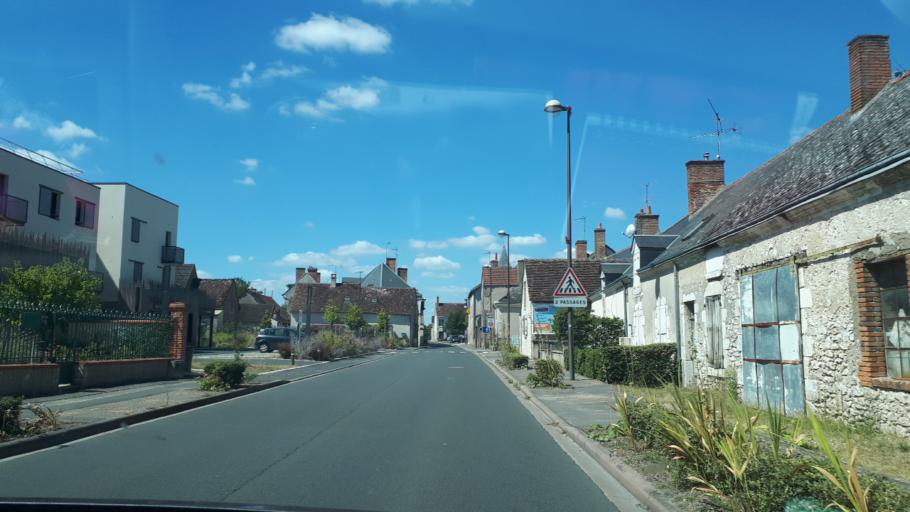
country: FR
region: Centre
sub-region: Departement du Loir-et-Cher
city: Mont-pres-Chambord
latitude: 47.5626
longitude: 1.4547
